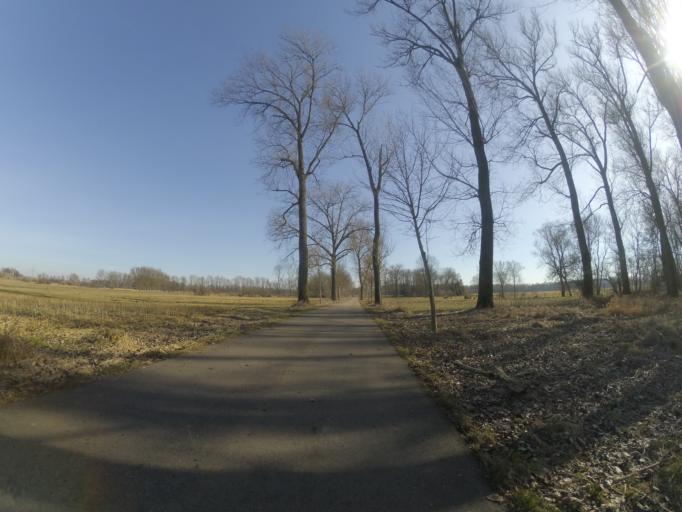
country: DE
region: Baden-Wuerttemberg
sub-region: Tuebingen Region
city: Rammingen
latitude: 48.4958
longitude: 10.1679
